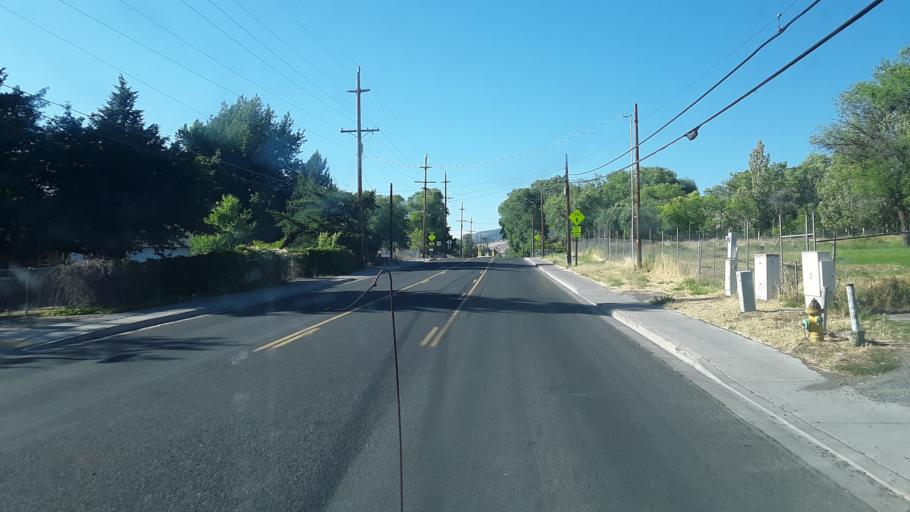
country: US
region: Oregon
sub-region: Klamath County
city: Altamont
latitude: 42.2020
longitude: -121.7377
